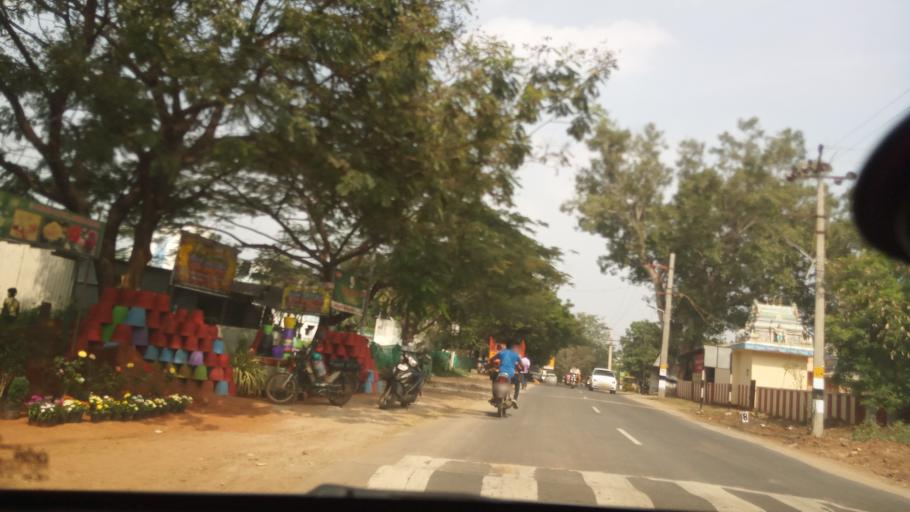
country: IN
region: Tamil Nadu
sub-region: Coimbatore
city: Perur
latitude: 11.0216
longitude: 76.8847
